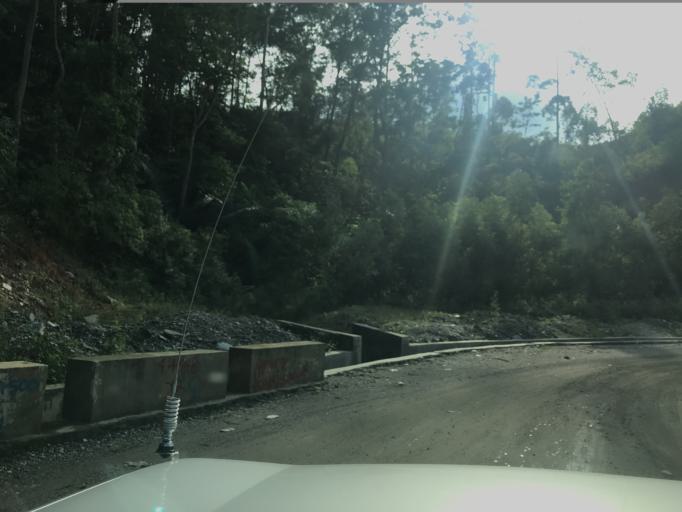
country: TL
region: Aileu
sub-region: Aileu Villa
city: Aileu
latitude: -8.6623
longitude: 125.5423
